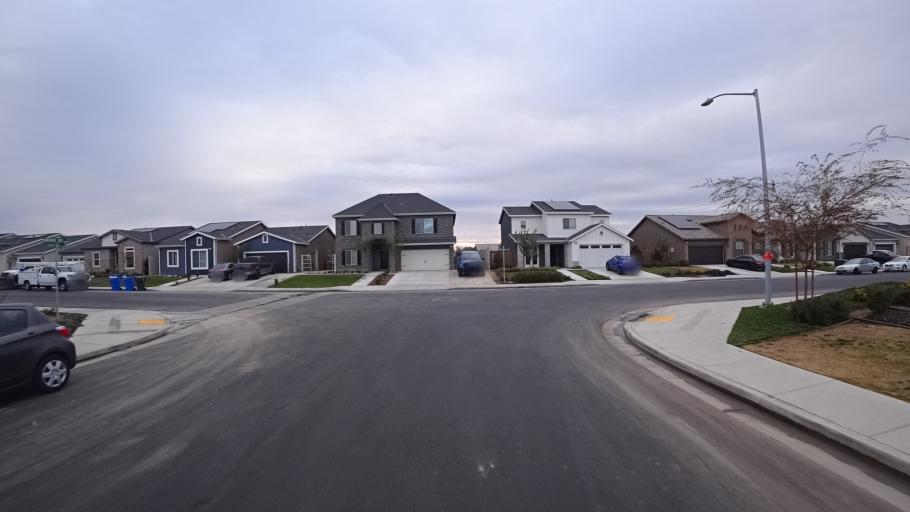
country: US
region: California
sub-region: Kern County
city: Greenfield
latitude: 35.2943
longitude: -119.0665
